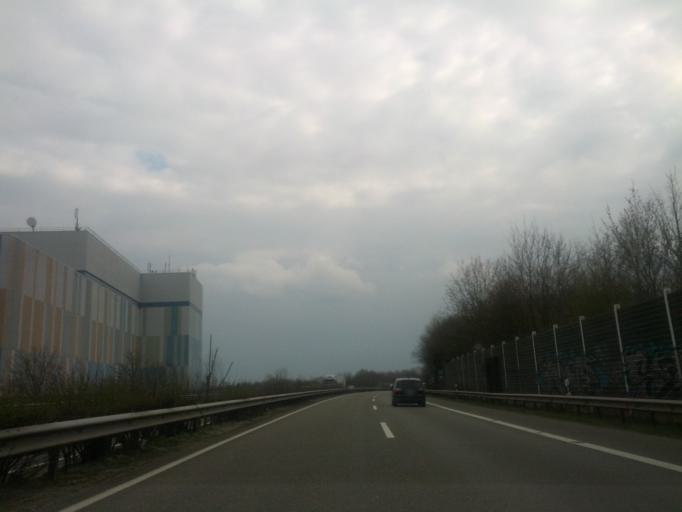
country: DE
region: Lower Saxony
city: Westerstede
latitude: 53.2641
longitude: 7.9359
